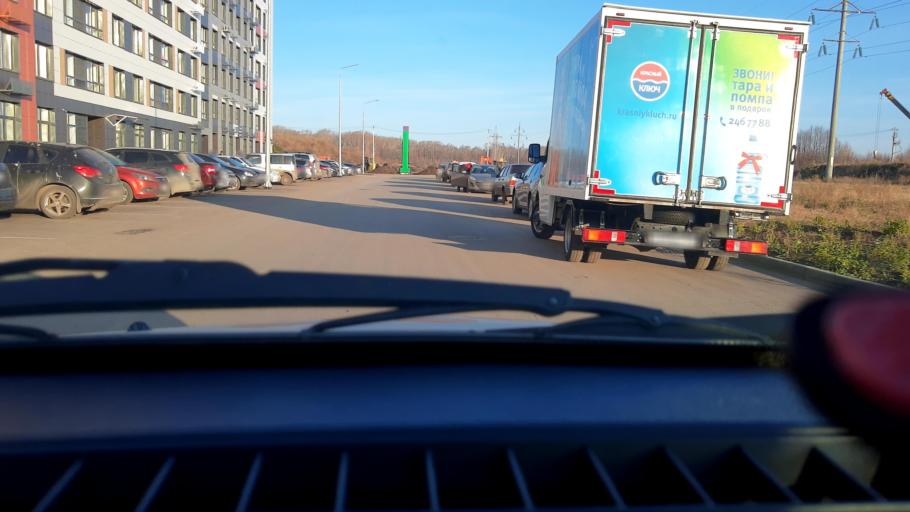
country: RU
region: Bashkortostan
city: Ufa
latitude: 54.6749
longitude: 55.9202
